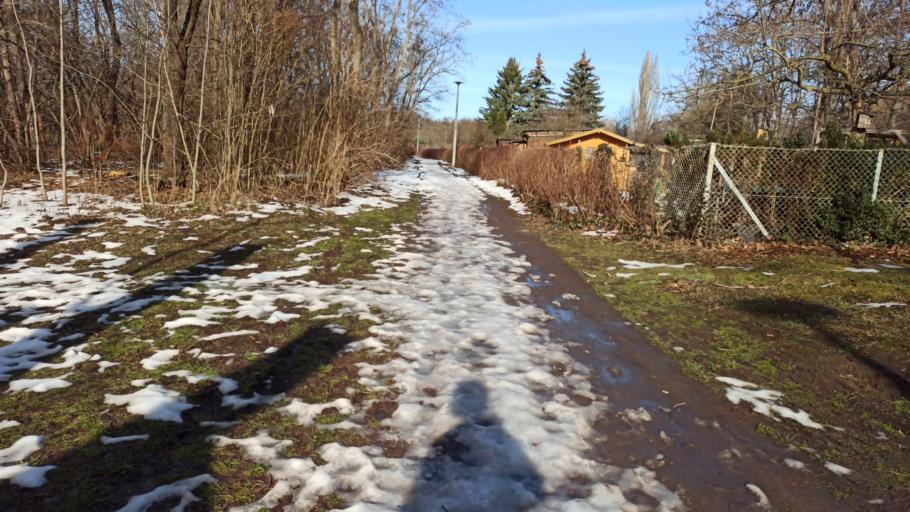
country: DE
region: Thuringia
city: Erfurt
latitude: 51.0171
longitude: 11.0172
